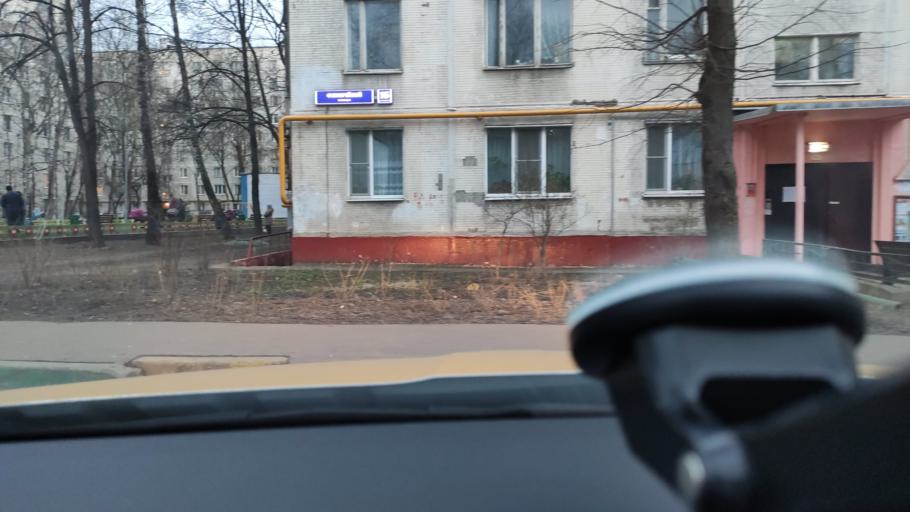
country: RU
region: Moscow
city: Khimki
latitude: 55.8581
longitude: 37.4405
